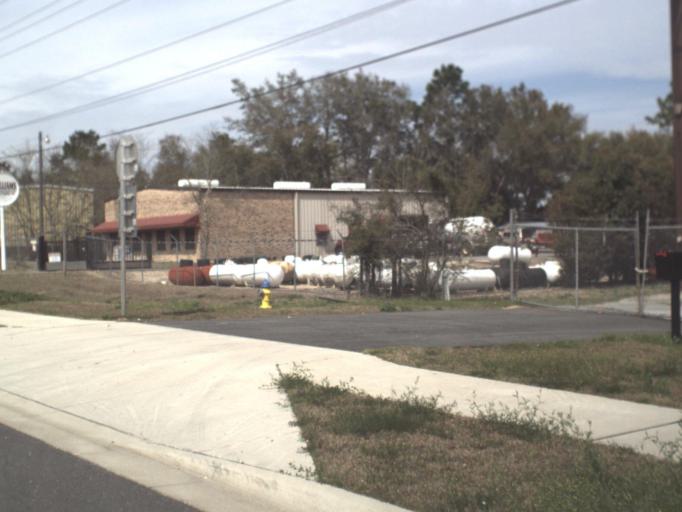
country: US
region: Florida
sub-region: Leon County
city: Tallahassee
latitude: 30.3759
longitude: -84.2796
